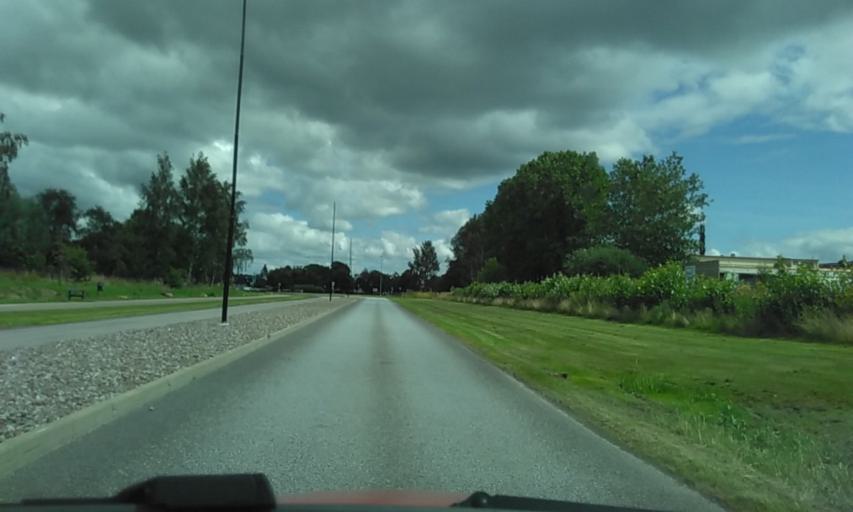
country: SE
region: Vaestra Goetaland
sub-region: Skara Kommun
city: Skara
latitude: 58.3823
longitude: 13.4224
